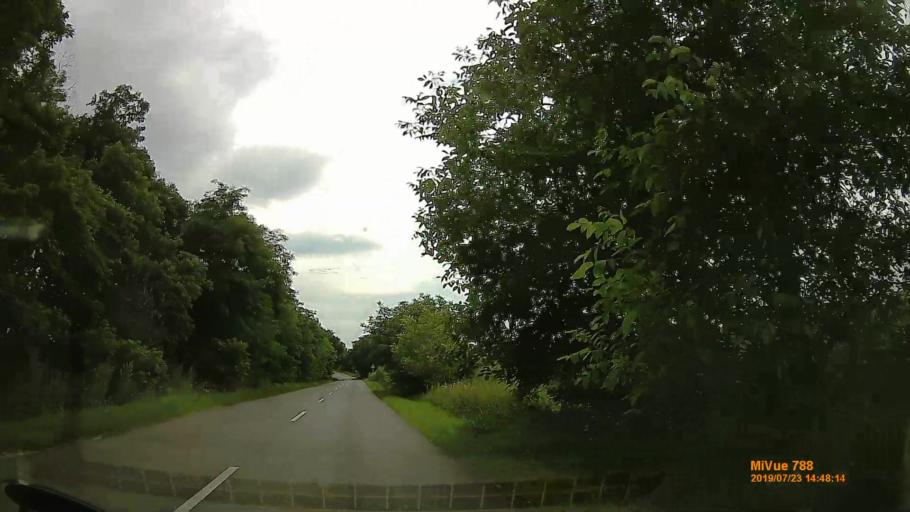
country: HU
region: Szabolcs-Szatmar-Bereg
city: Nyiregyhaza
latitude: 47.9050
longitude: 21.6707
